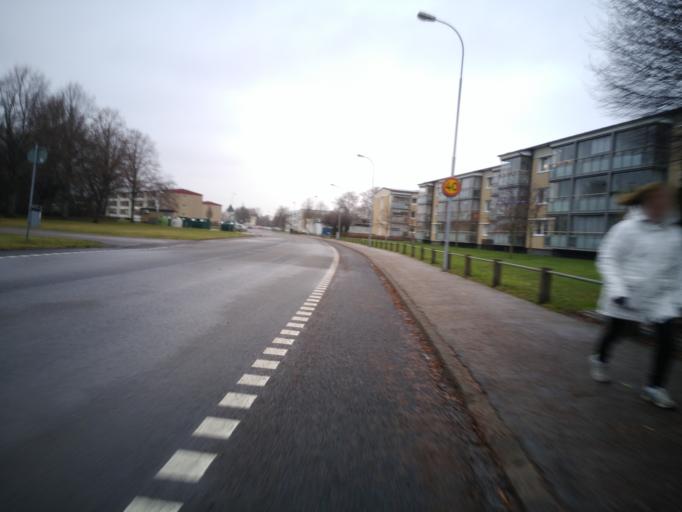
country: SE
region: Vaestra Goetaland
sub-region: Lidkopings Kommun
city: Lidkoping
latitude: 58.4911
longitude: 13.1551
